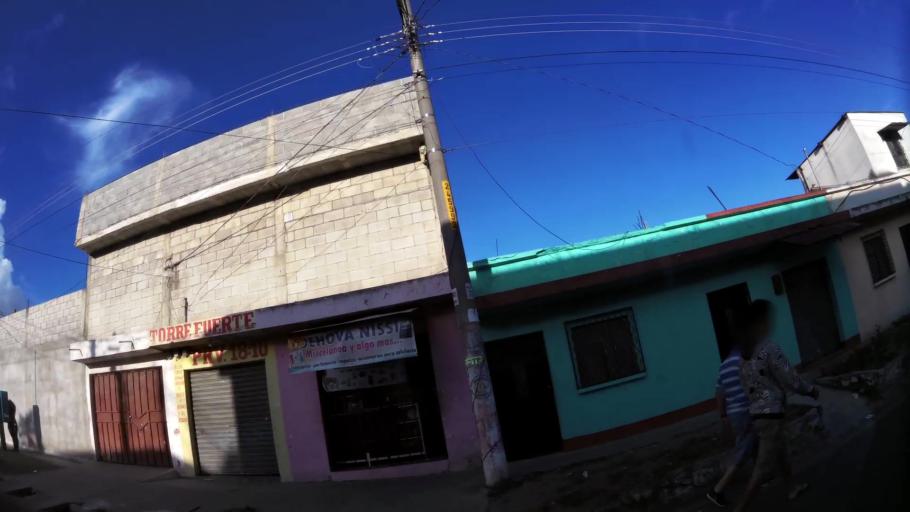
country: GT
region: Guatemala
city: Villa Nueva
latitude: 14.5204
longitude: -90.5864
